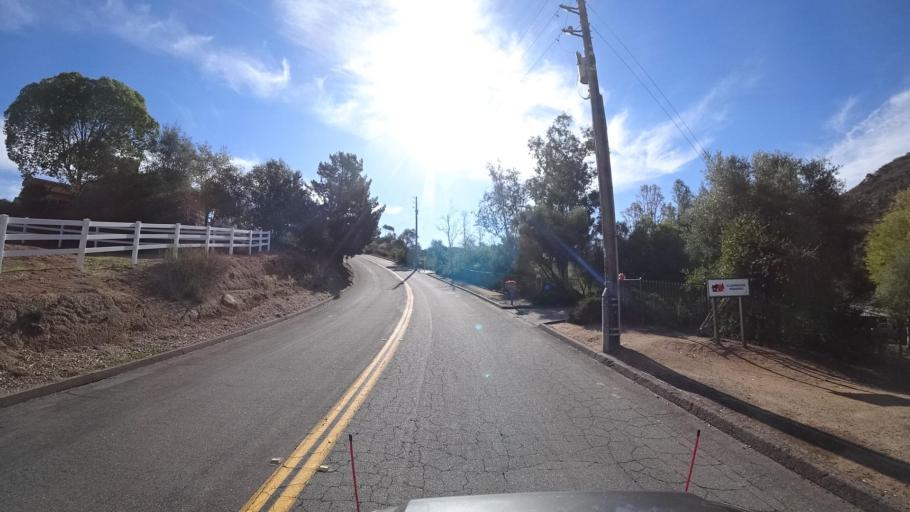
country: US
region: California
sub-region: San Diego County
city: Alpine
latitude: 32.8136
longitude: -116.7361
